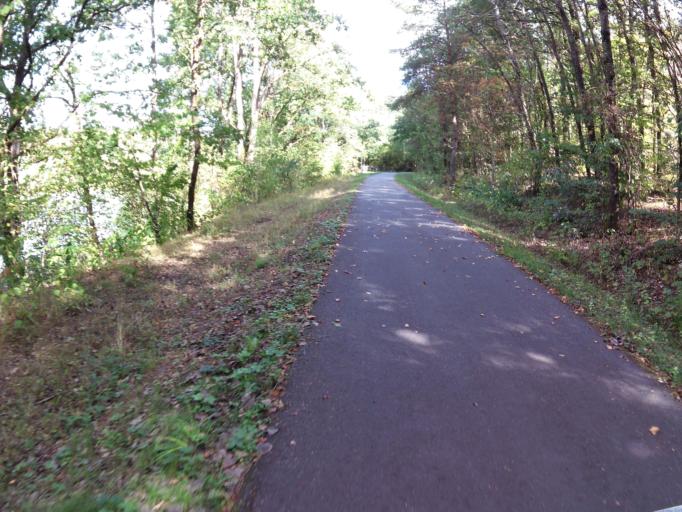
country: DE
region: Rheinland-Pfalz
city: Arzfeld
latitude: 50.0770
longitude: 6.2641
